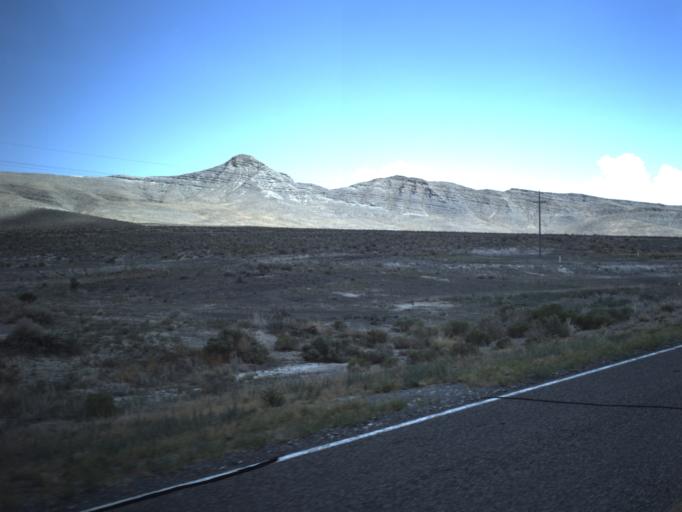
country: US
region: Utah
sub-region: Beaver County
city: Milford
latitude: 39.0437
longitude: -113.4066
